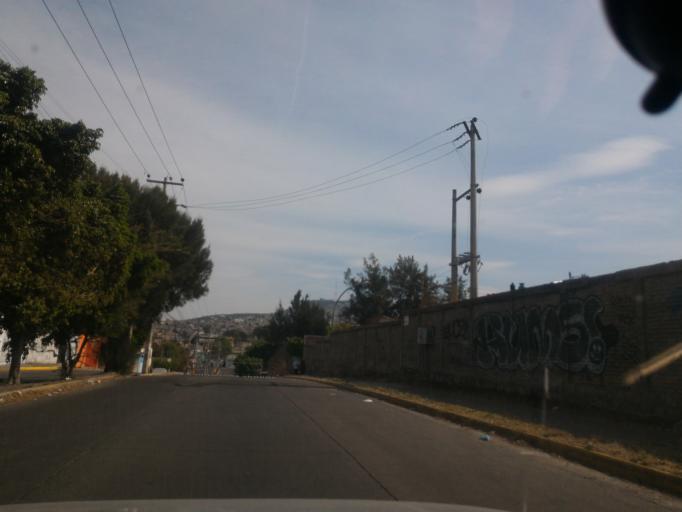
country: MX
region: Jalisco
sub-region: Tlajomulco de Zuniga
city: Altus Bosques
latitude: 20.6169
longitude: -103.3832
